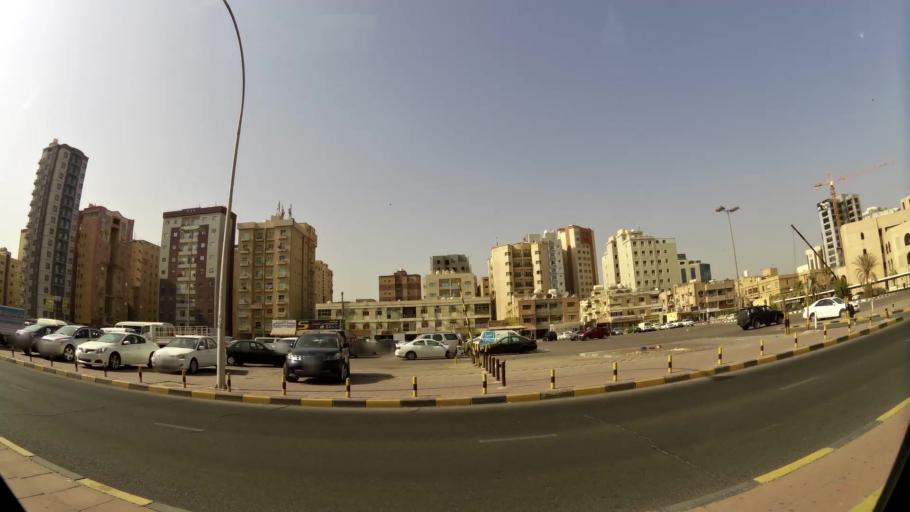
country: KW
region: Muhafazat Hawalli
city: Hawalli
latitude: 29.3310
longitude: 48.0104
